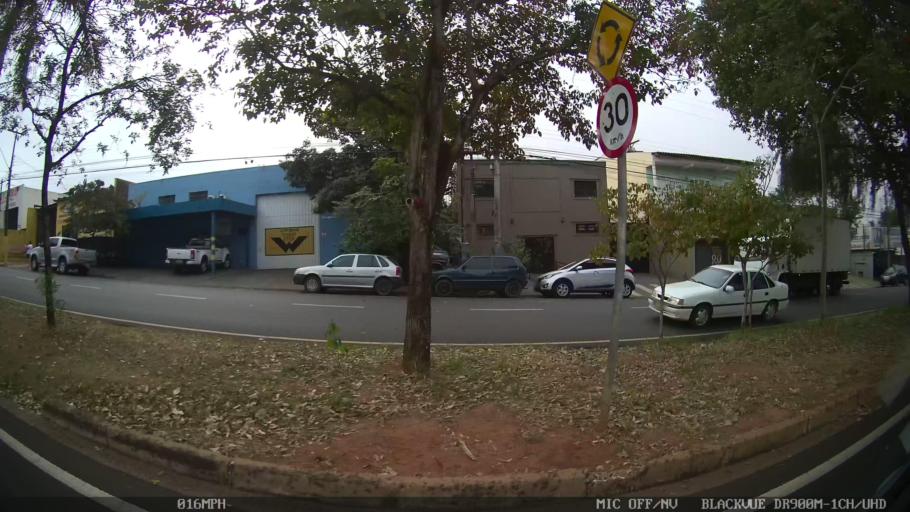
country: BR
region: Sao Paulo
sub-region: Sao Jose Do Rio Preto
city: Sao Jose do Rio Preto
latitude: -20.8460
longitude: -49.3700
